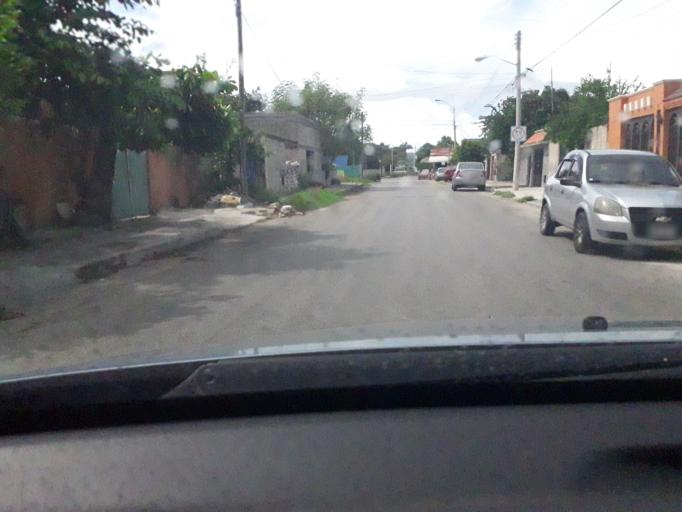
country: MX
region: Yucatan
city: Merida
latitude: 20.9653
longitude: -89.6575
